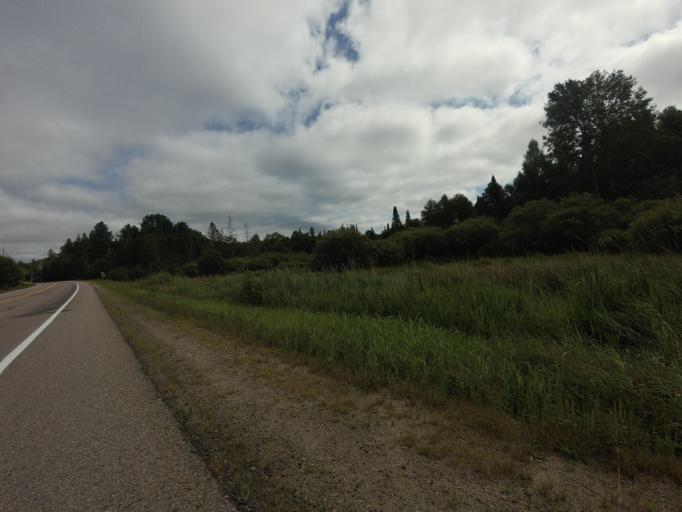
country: CA
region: Ontario
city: Bancroft
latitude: 44.9063
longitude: -78.4121
